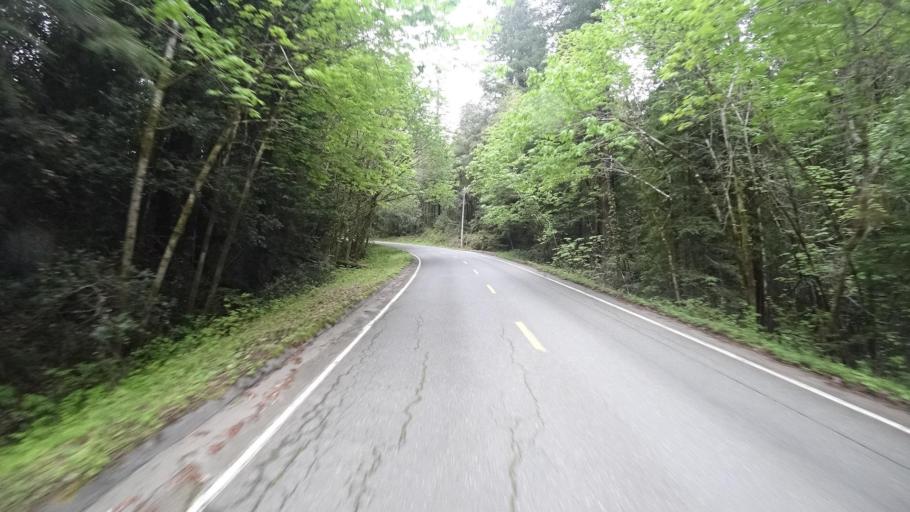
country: US
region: California
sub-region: Humboldt County
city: Redway
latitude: 40.3229
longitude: -123.9256
